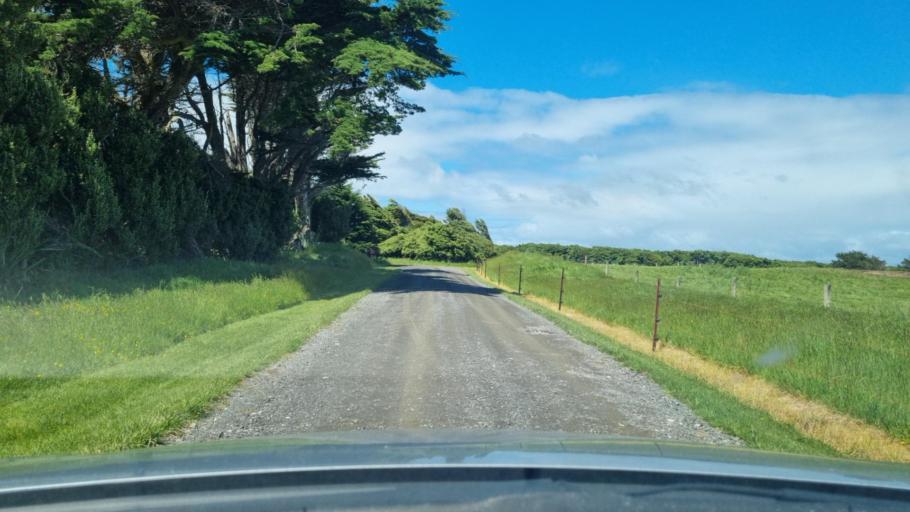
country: NZ
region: Southland
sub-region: Invercargill City
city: Invercargill
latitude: -46.4447
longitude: 168.2784
